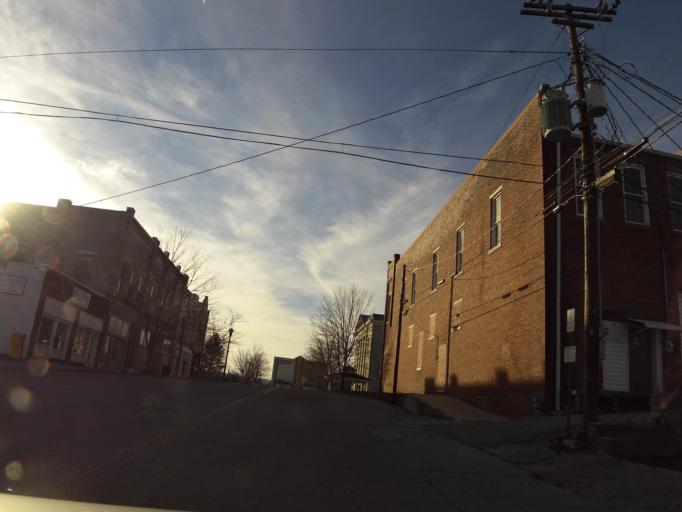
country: US
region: Tennessee
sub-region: White County
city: Sparta
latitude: 35.9250
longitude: -85.4634
